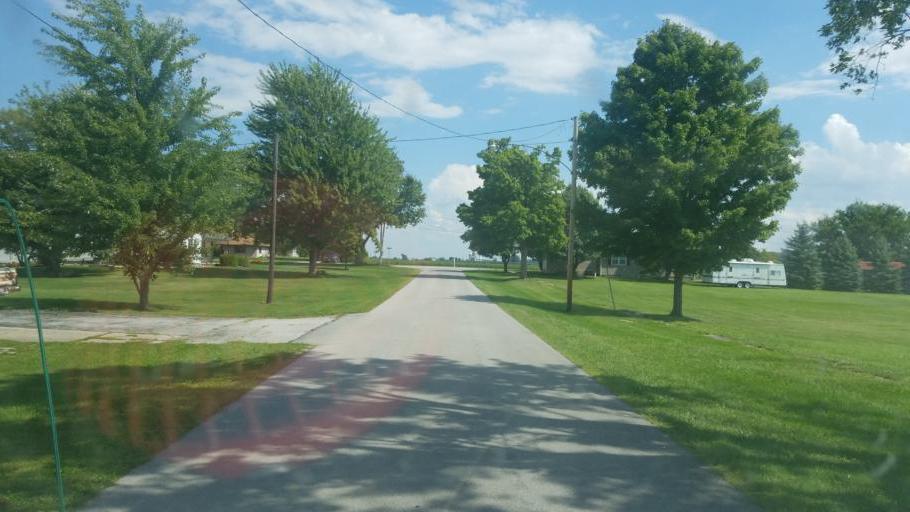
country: US
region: Ohio
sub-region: Hardin County
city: Forest
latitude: 40.8604
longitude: -83.4587
